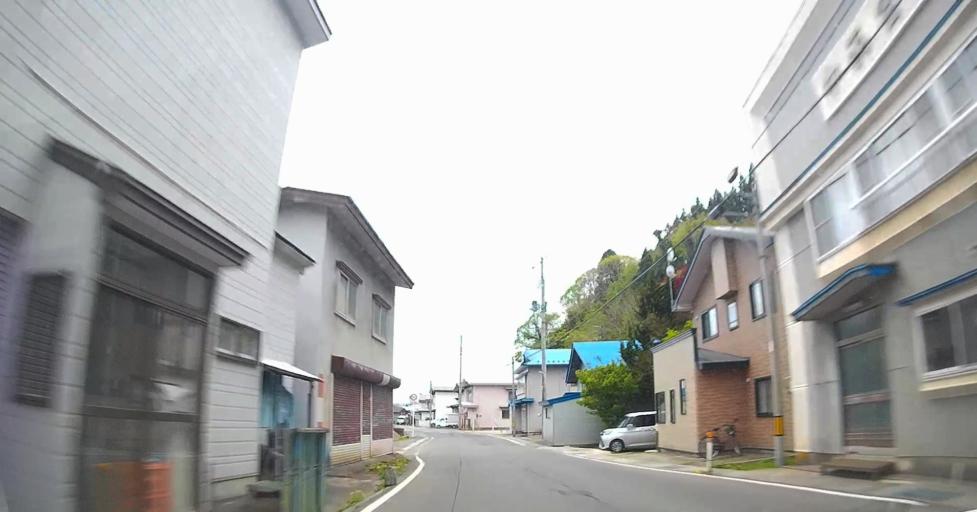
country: JP
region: Aomori
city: Shimokizukuri
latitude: 41.2034
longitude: 140.4277
